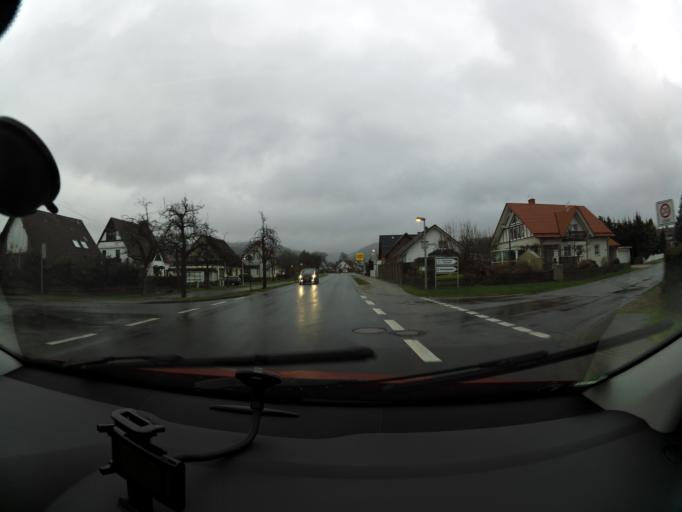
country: DE
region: Lower Saxony
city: Herzberg am Harz
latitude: 51.6552
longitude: 10.3495
